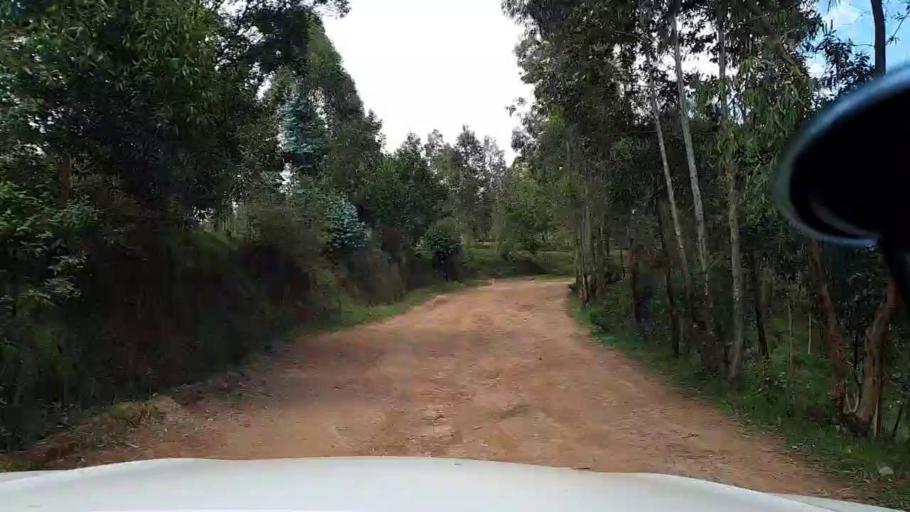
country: RW
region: Kigali
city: Kigali
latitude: -1.7885
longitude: 29.8285
